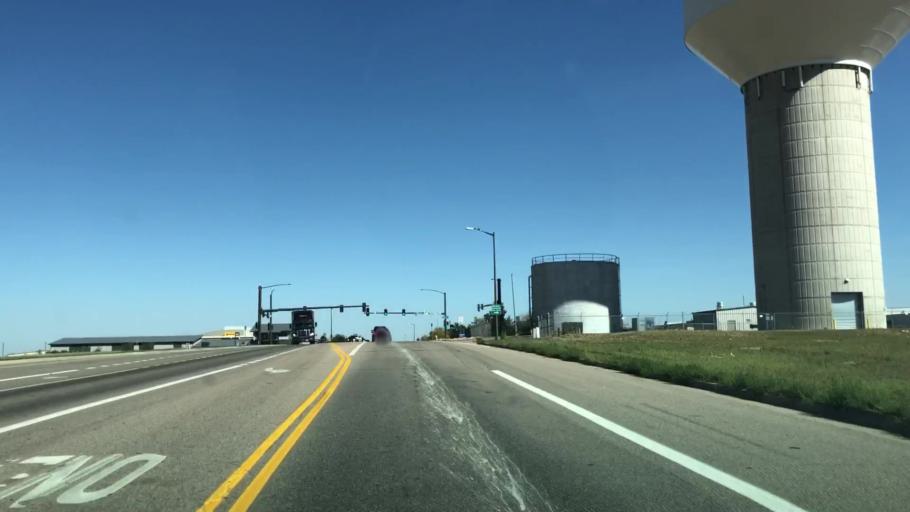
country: US
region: Colorado
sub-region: Weld County
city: Windsor
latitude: 40.4359
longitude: -104.9752
